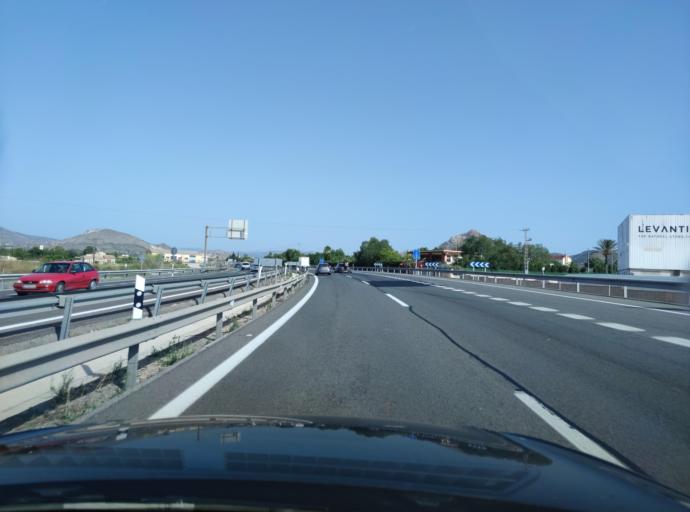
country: ES
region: Valencia
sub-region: Provincia de Alicante
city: Novelda
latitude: 38.3946
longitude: -0.7477
